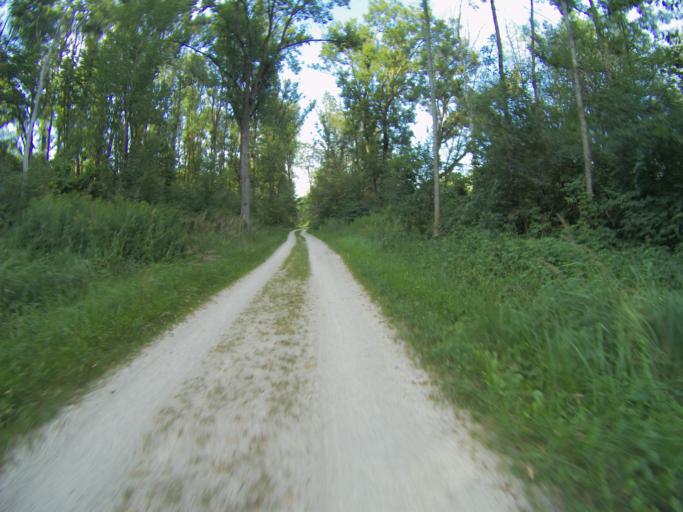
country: DE
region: Bavaria
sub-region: Upper Bavaria
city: Hallbergmoos
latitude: 48.3474
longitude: 11.7160
